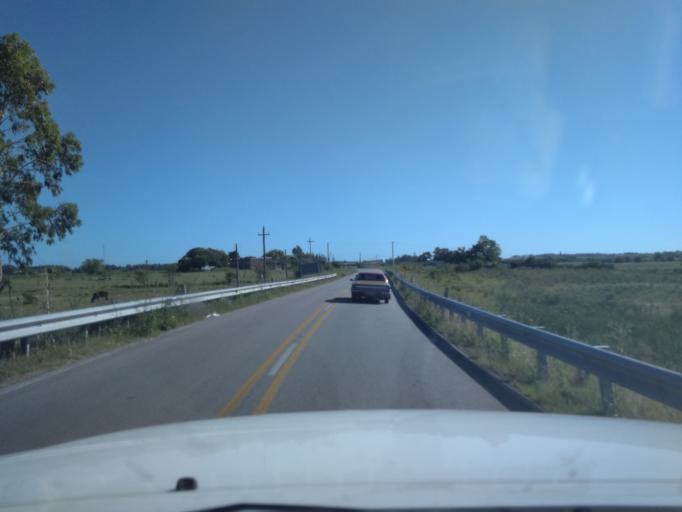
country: UY
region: Canelones
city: San Ramon
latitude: -34.3213
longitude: -55.9612
